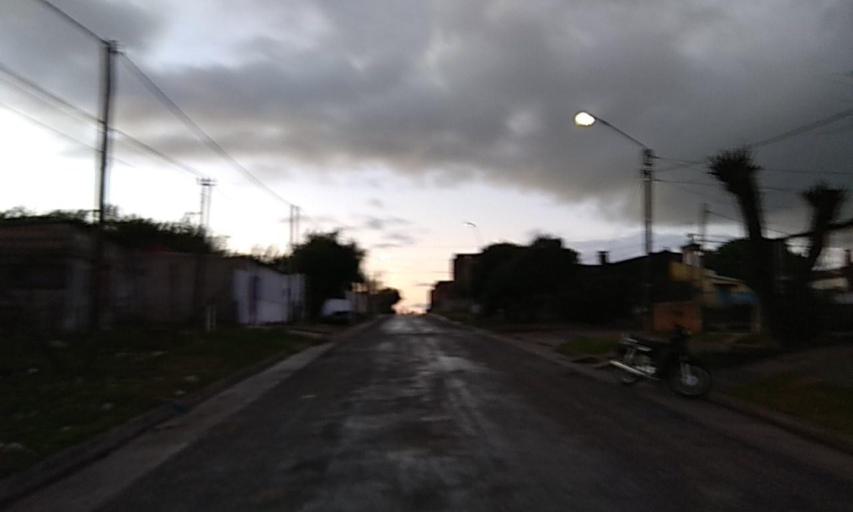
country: UY
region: Florida
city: Florida
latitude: -34.1100
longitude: -56.2098
